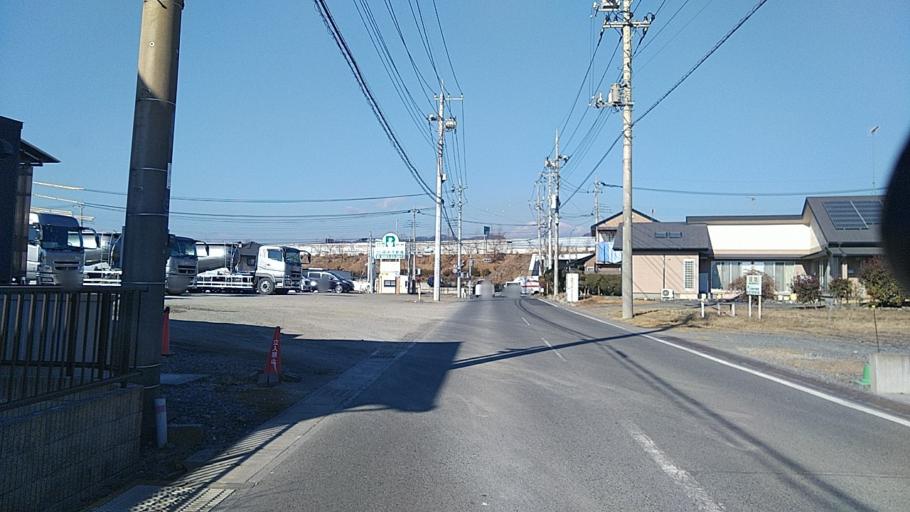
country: JP
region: Tochigi
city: Tanuma
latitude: 36.3633
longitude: 139.5594
